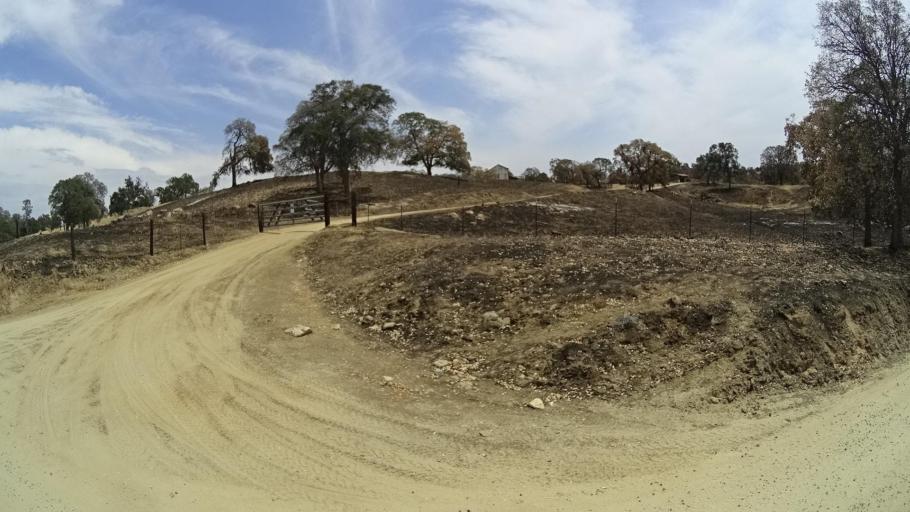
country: US
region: California
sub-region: Madera County
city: Ahwahnee
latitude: 37.3589
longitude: -119.8701
